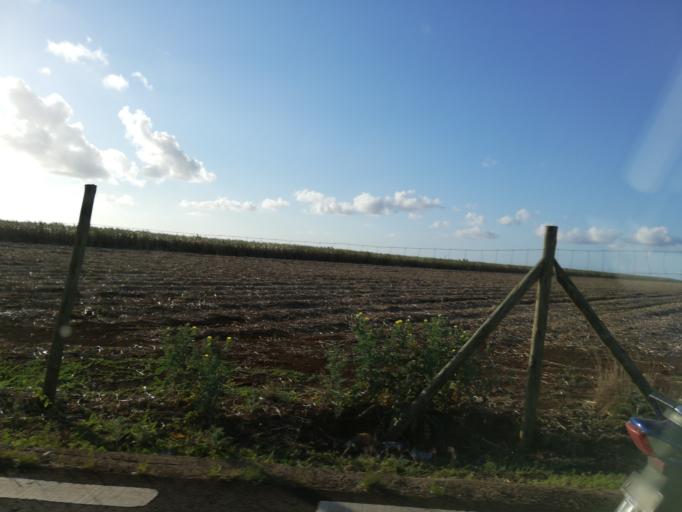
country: MU
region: Pamplemousses
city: Grande Pointe aux Piments
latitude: -20.0812
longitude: 57.5272
